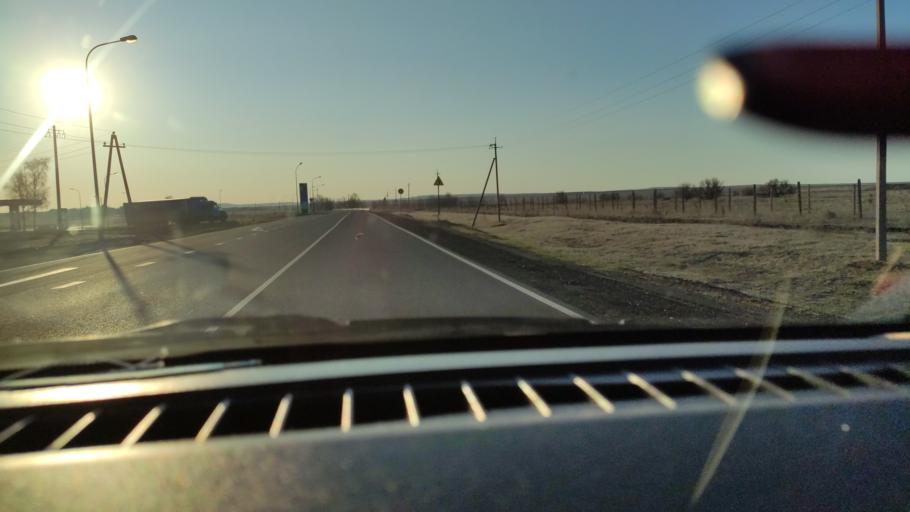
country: RU
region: Saratov
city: Sennoy
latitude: 52.1504
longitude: 46.9773
